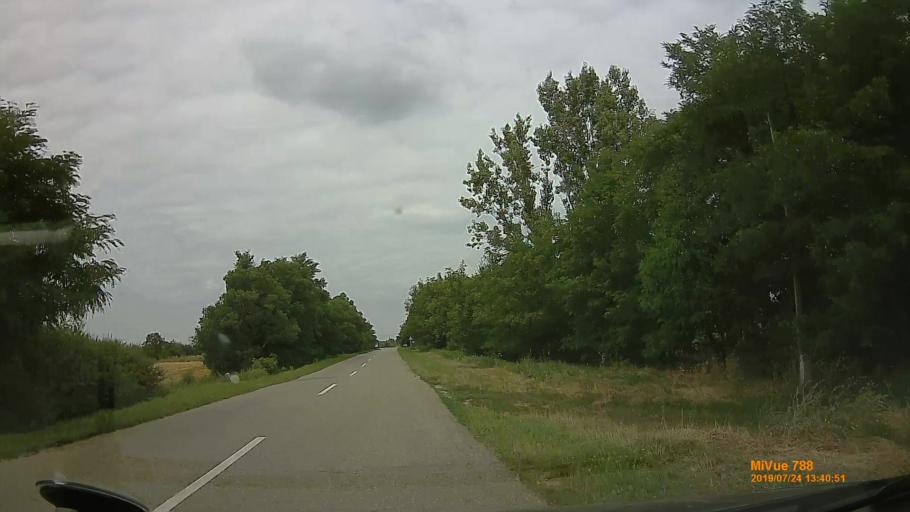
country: HU
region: Szabolcs-Szatmar-Bereg
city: Aranyosapati
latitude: 48.2561
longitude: 22.3147
